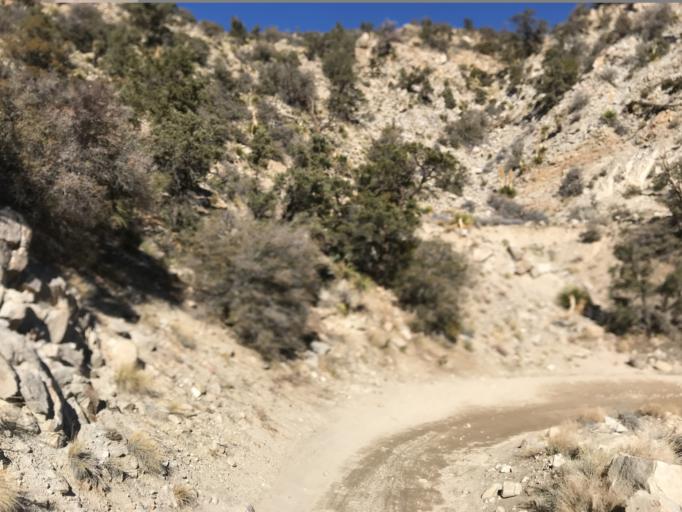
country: US
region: California
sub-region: San Bernardino County
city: Big Bear City
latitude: 34.2324
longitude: -116.6817
